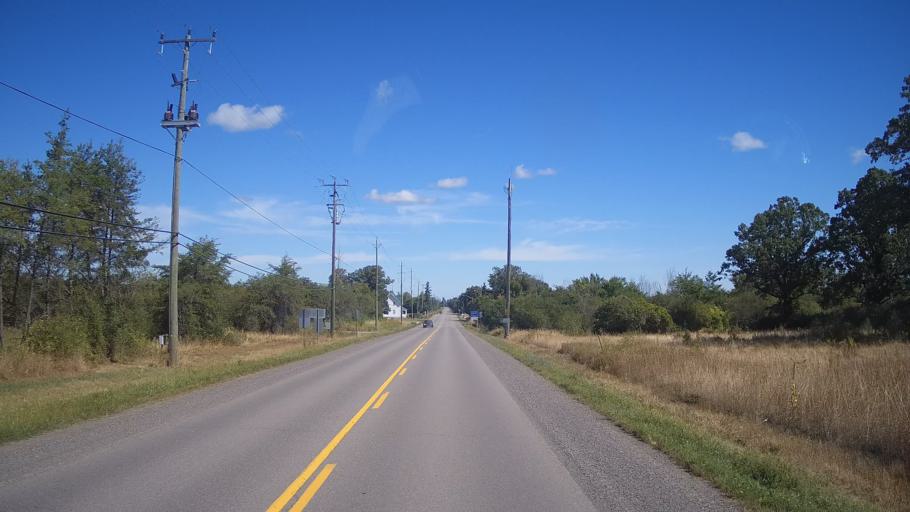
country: CA
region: Ontario
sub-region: Lanark County
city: Smiths Falls
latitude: 44.9235
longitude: -75.8374
